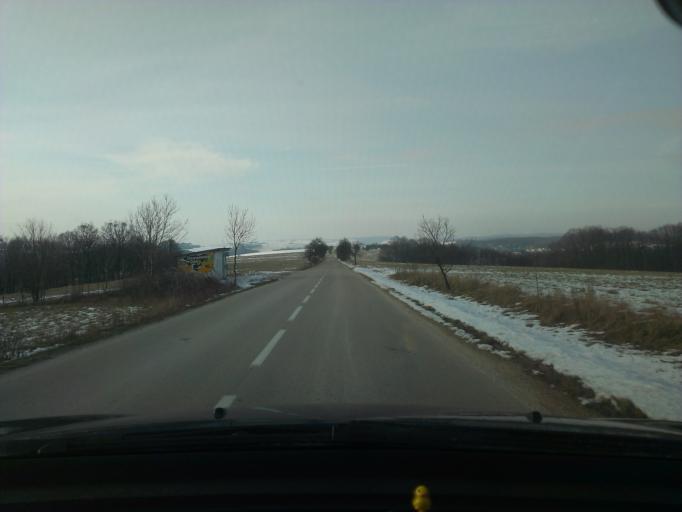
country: SK
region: Nitriansky
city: Stara Tura
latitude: 48.7425
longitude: 17.6478
